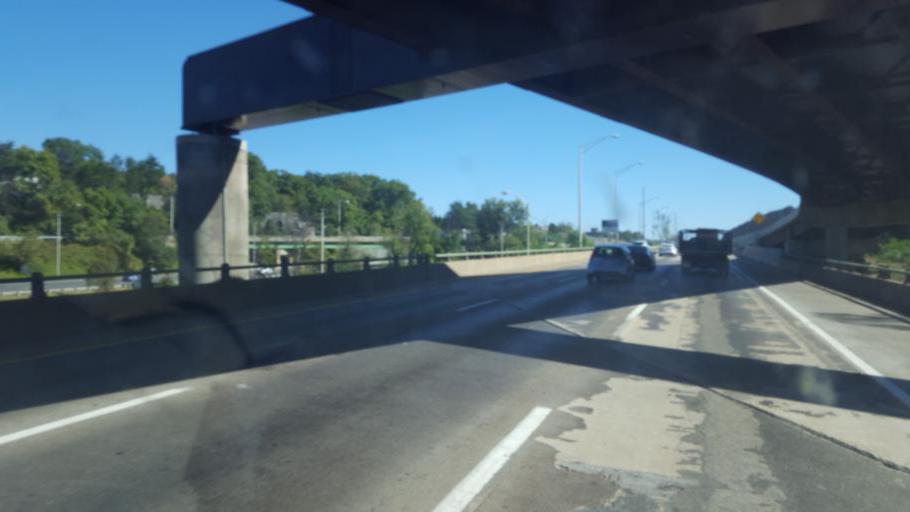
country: US
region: Virginia
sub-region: Fairfax County
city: Lincolnia
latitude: 38.8103
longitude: -77.1498
